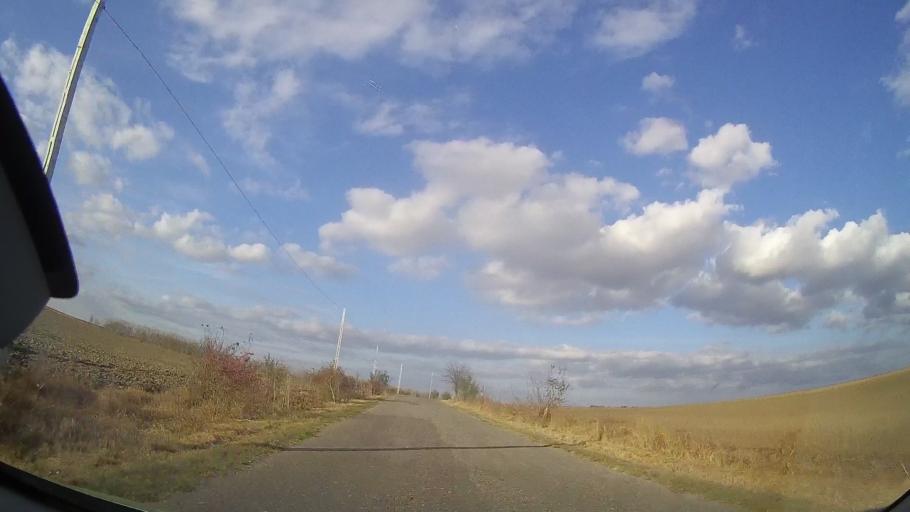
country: RO
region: Constanta
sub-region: Comuna Cerchezu
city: Cerchezu
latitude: 43.8451
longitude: 28.0985
